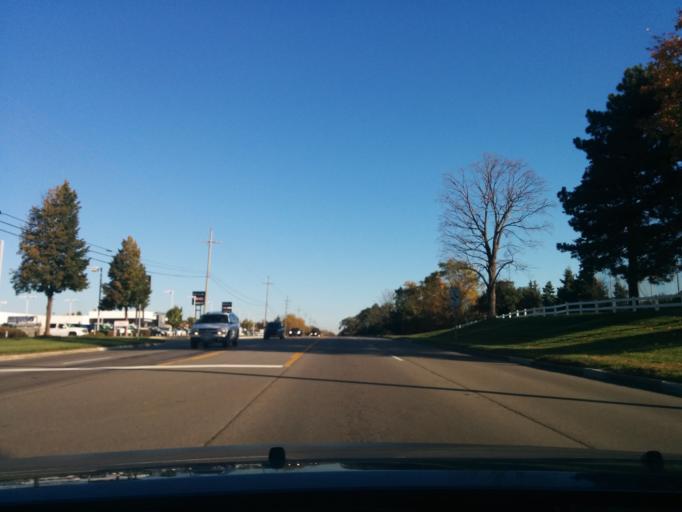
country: US
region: Michigan
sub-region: Wayne County
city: Plymouth
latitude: 42.3901
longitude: -83.4812
